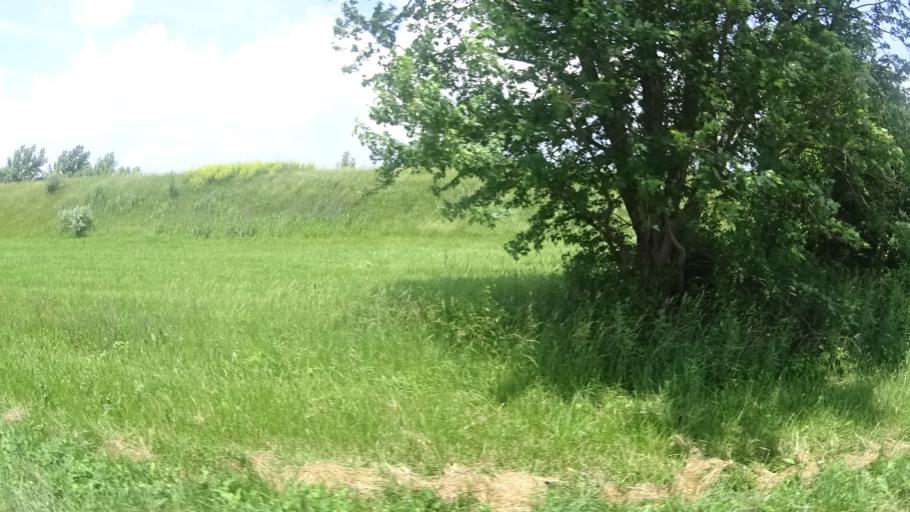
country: US
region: Ohio
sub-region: Huron County
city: Bellevue
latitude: 41.3250
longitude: -82.7732
